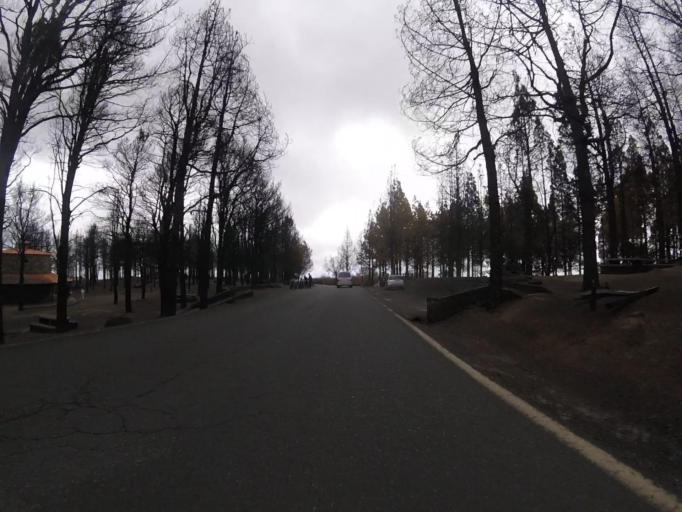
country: ES
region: Canary Islands
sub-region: Provincia de Las Palmas
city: Tejeda
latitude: 27.9875
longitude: -15.5784
